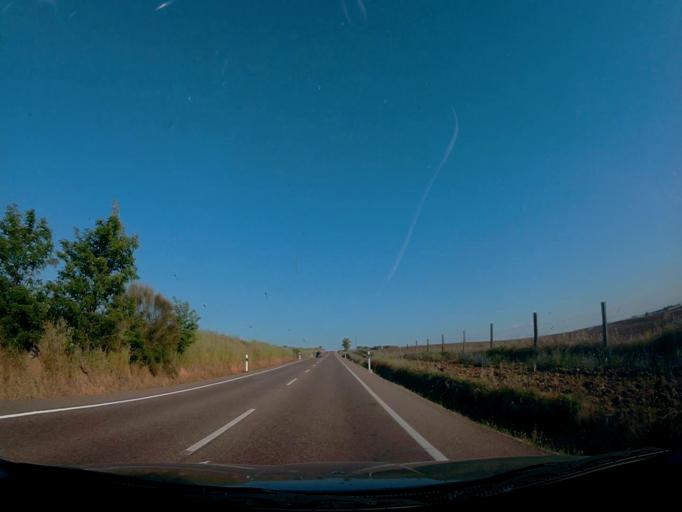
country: ES
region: Castille-La Mancha
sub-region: Province of Toledo
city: Maqueda
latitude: 40.1020
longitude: -4.3954
